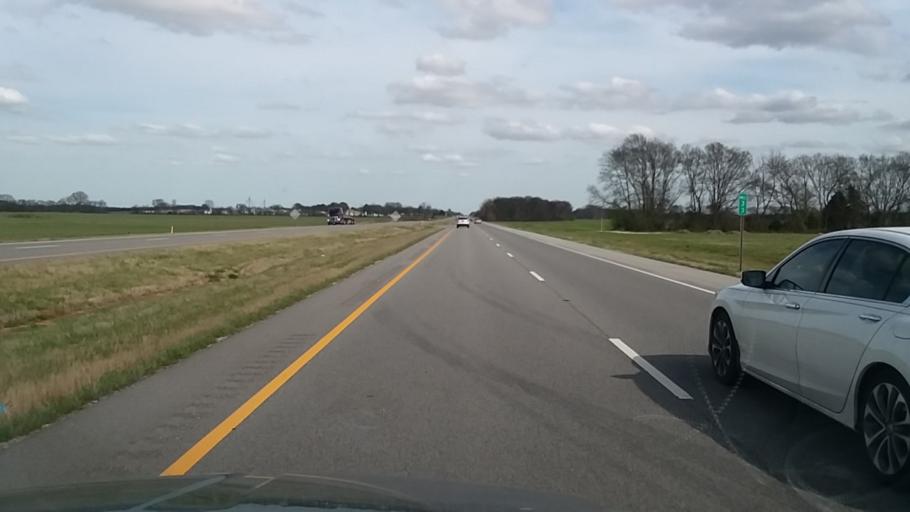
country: US
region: Alabama
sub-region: Colbert County
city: Muscle Shoals
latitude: 34.6850
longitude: -87.5834
